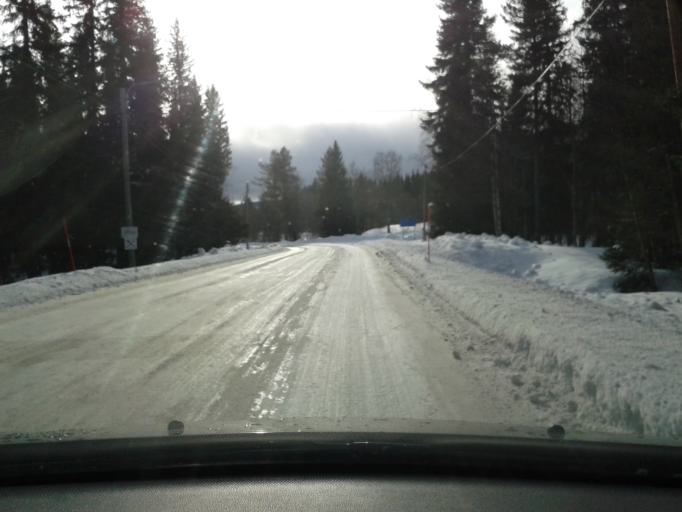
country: SE
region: Vaesterbotten
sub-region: Vilhelmina Kommun
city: Sjoberg
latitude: 64.6950
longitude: 16.2655
